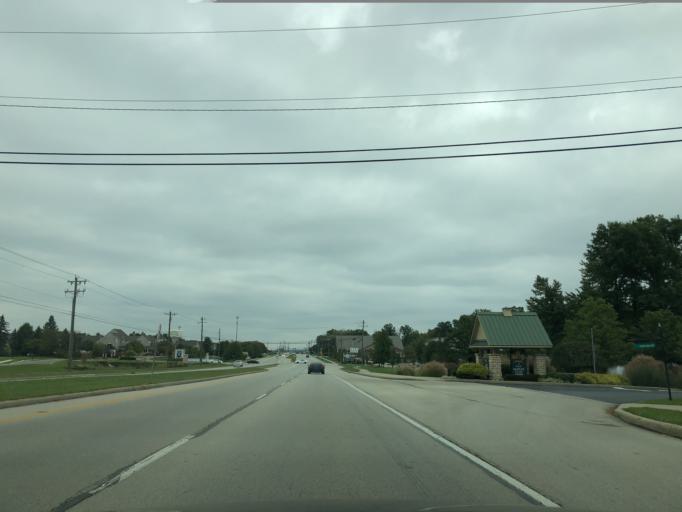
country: US
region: Ohio
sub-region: Warren County
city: Landen
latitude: 39.2987
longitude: -84.2884
